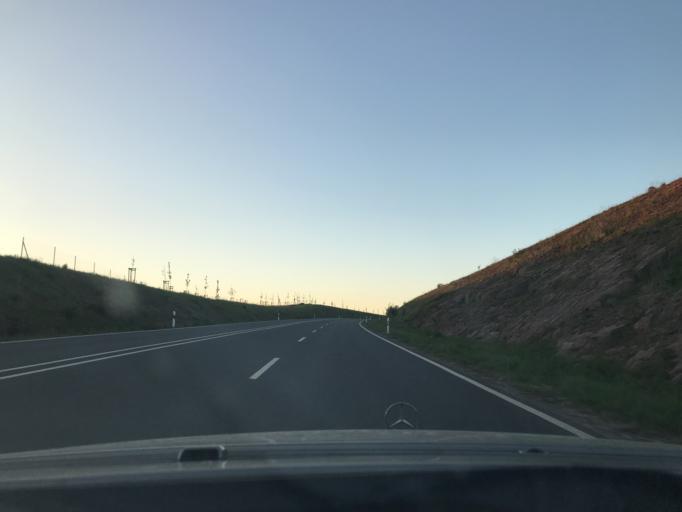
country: DE
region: Thuringia
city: Heilbad Heiligenstadt
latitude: 51.3781
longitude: 10.1145
